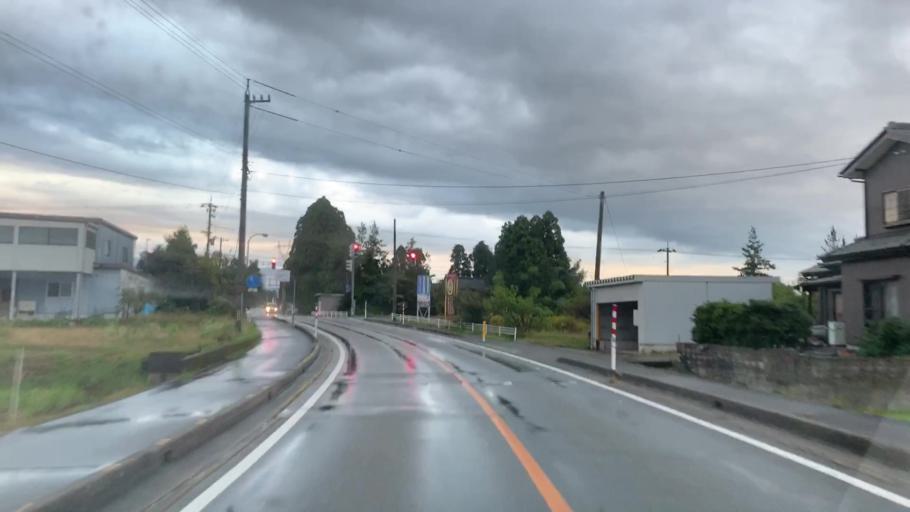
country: JP
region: Toyama
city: Kamiichi
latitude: 36.6626
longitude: 137.3272
